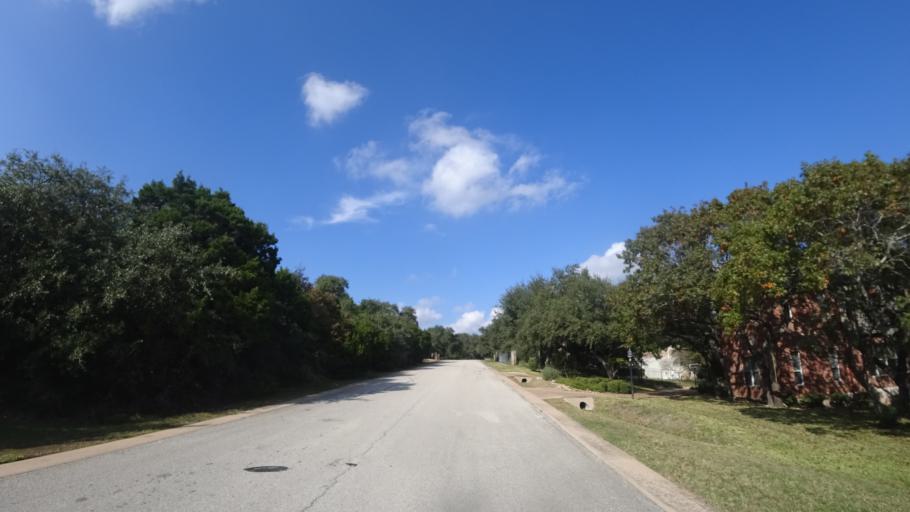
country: US
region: Texas
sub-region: Travis County
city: Lost Creek
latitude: 30.3038
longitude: -97.8508
